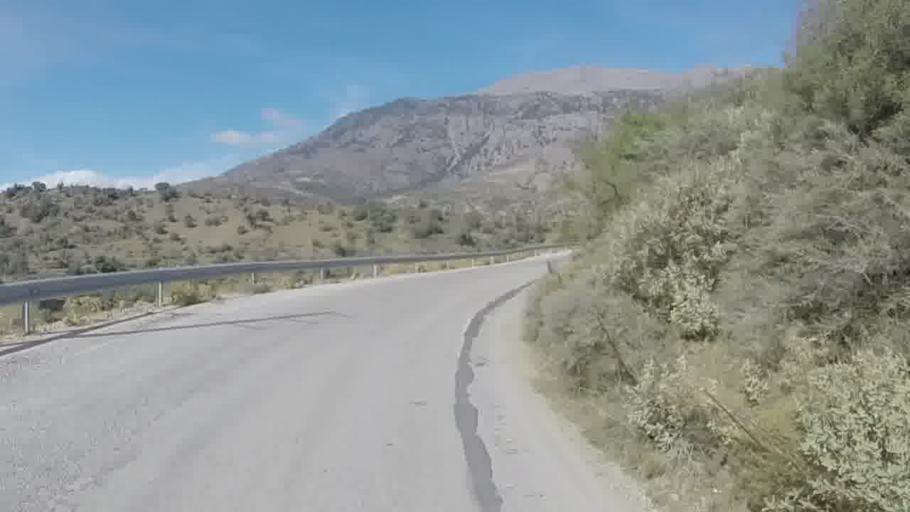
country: GR
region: Crete
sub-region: Nomos Rethymnis
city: Agia Galini
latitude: 35.1761
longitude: 24.7360
